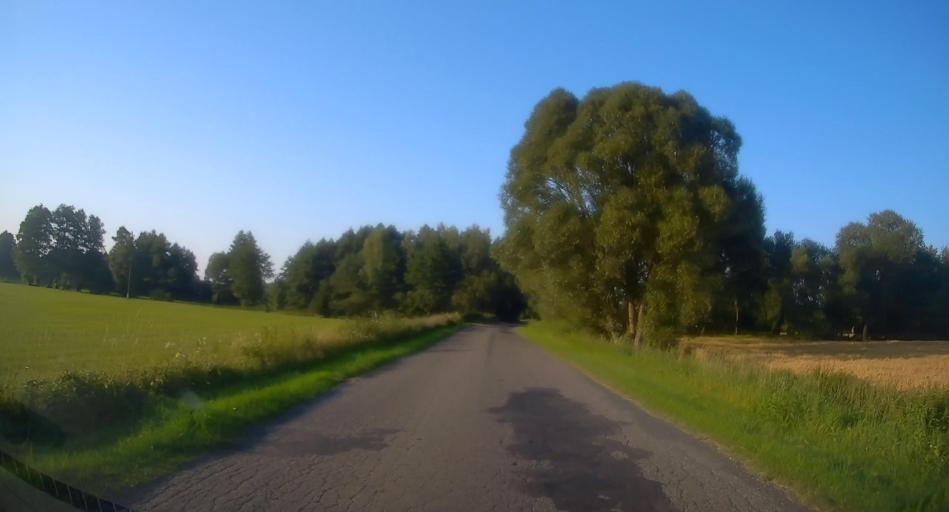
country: PL
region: Lodz Voivodeship
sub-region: Powiat skierniewicki
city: Kaweczyn Nowy
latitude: 51.8952
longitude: 20.2971
